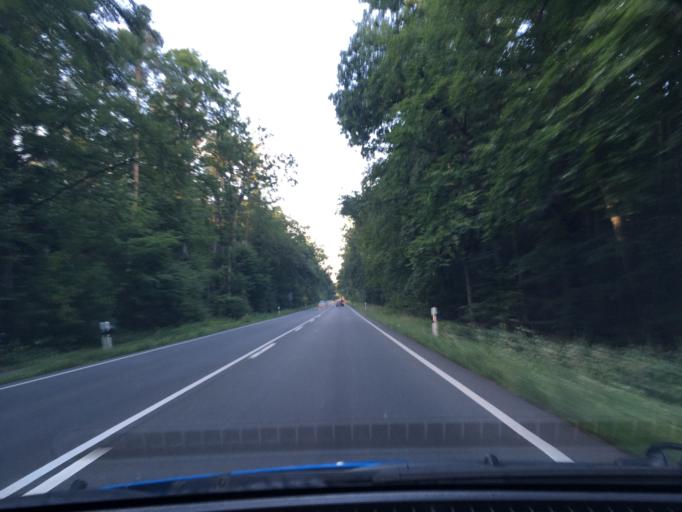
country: DE
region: Lower Saxony
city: Suderburg
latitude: 52.8903
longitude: 10.5082
